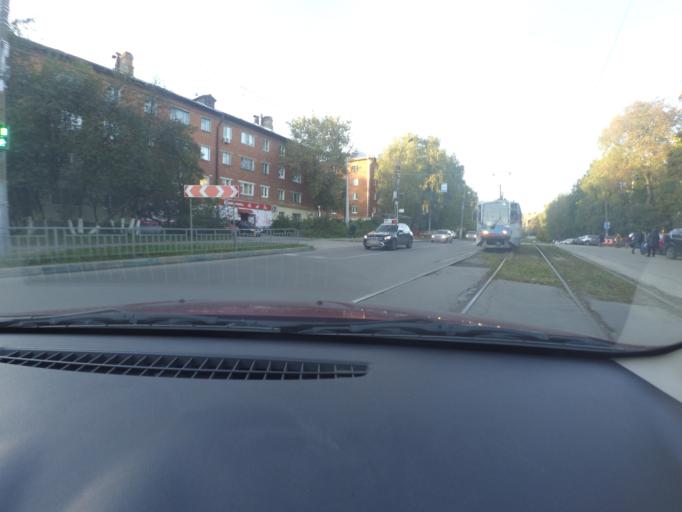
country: RU
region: Nizjnij Novgorod
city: Nizhniy Novgorod
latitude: 56.2758
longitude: 43.9893
